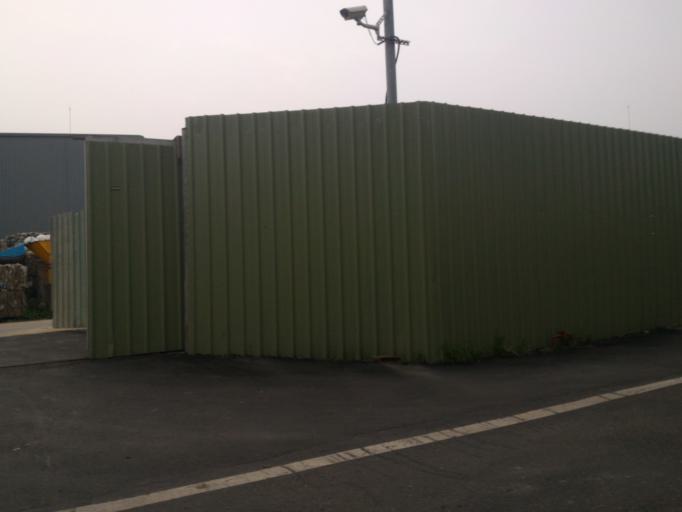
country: TW
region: Taipei
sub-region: Taipei
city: Banqiao
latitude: 24.9577
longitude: 121.4089
